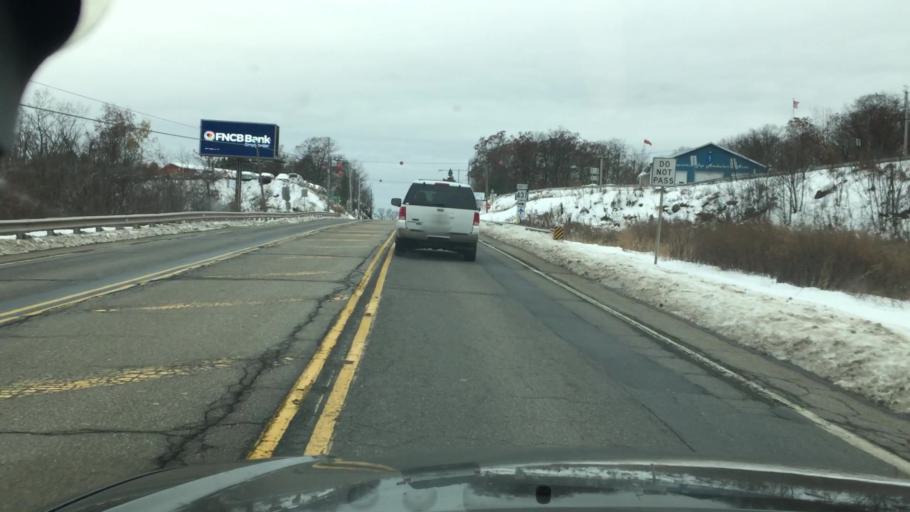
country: US
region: Pennsylvania
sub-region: Luzerne County
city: Mountain Top
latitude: 41.1741
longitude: -75.8800
